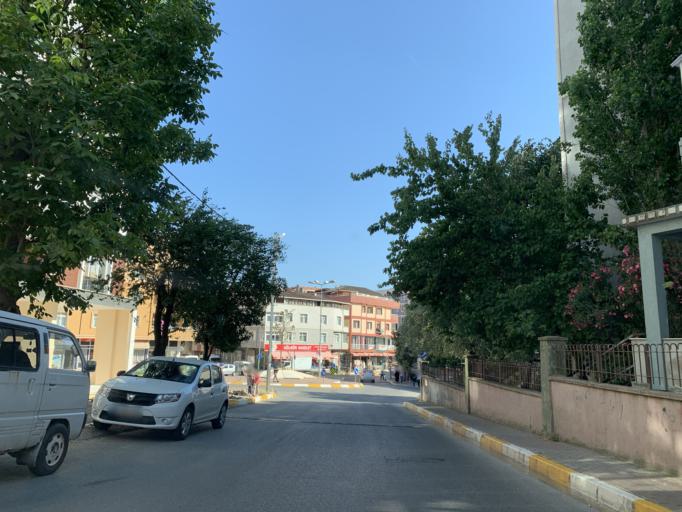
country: TR
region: Istanbul
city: Pendik
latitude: 40.8836
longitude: 29.2684
